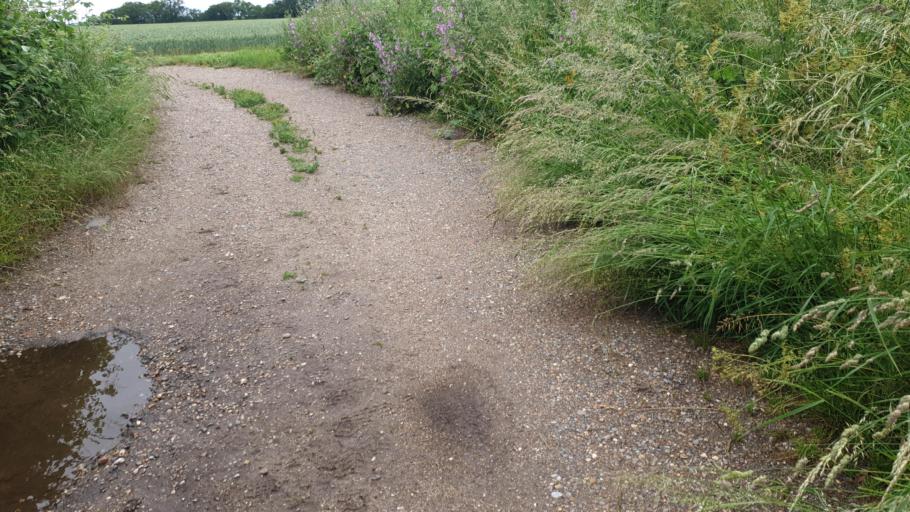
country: GB
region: England
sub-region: Essex
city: Great Bentley
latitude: 51.8851
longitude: 1.0982
